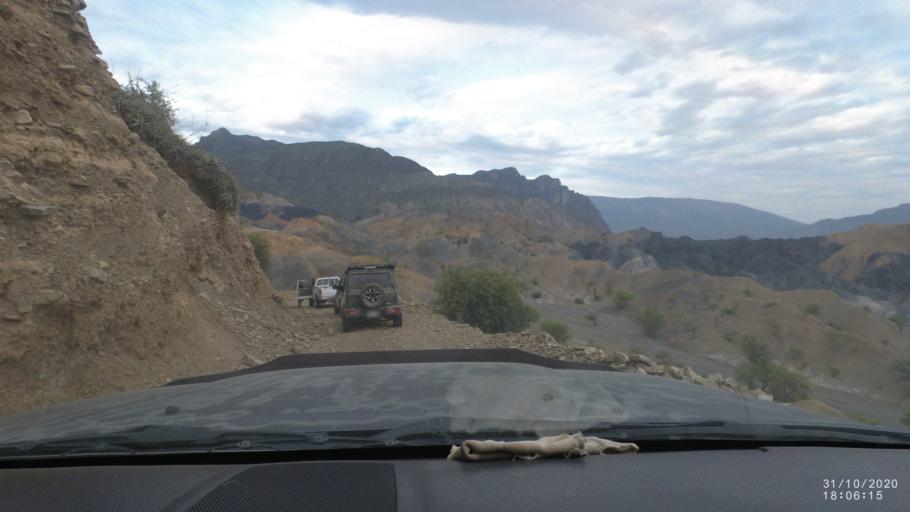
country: BO
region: Chuquisaca
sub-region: Provincia Zudanez
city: Mojocoya
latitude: -18.6661
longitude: -64.5284
